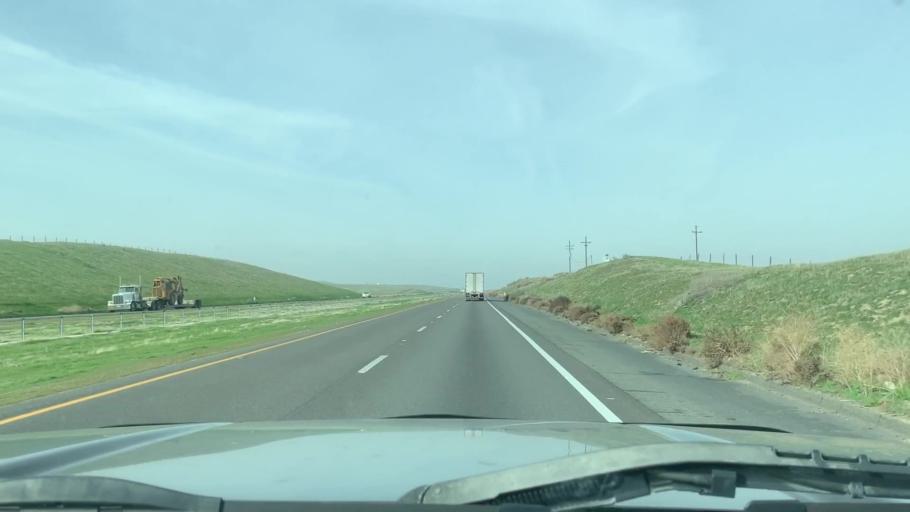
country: US
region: California
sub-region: Kings County
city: Kettleman City
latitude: 36.0424
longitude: -120.0438
